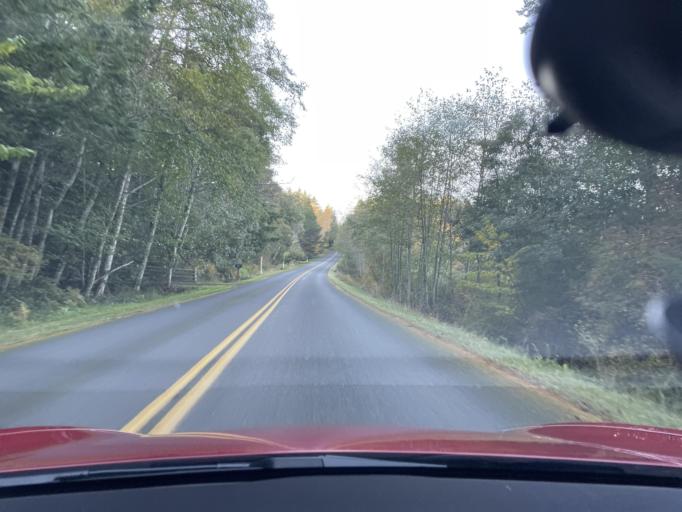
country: US
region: Washington
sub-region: San Juan County
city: Friday Harbor
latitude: 48.5590
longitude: -123.1644
